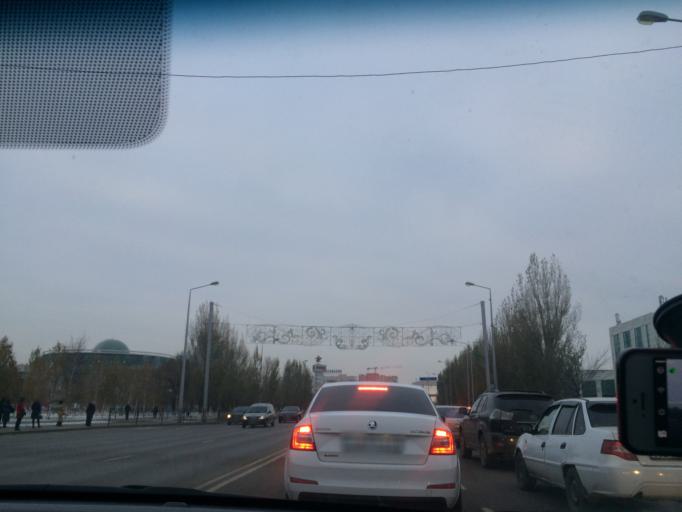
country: KZ
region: Astana Qalasy
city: Astana
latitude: 51.1485
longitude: 71.4124
